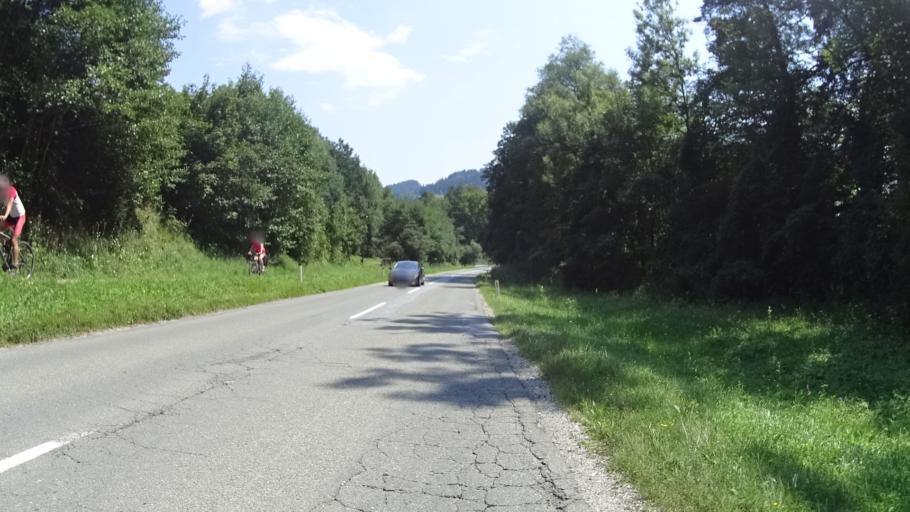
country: SI
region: Mezica
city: Mezica
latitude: 46.5475
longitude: 14.8678
